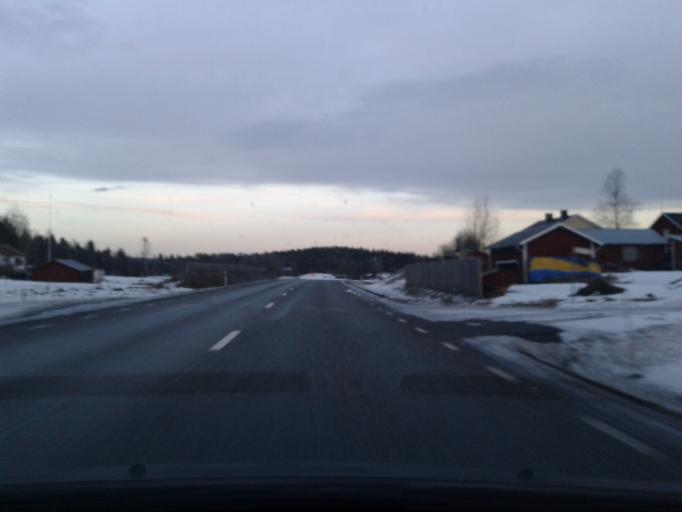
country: SE
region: Vaesternorrland
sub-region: Kramfors Kommun
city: Bollstabruk
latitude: 63.0768
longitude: 17.5496
